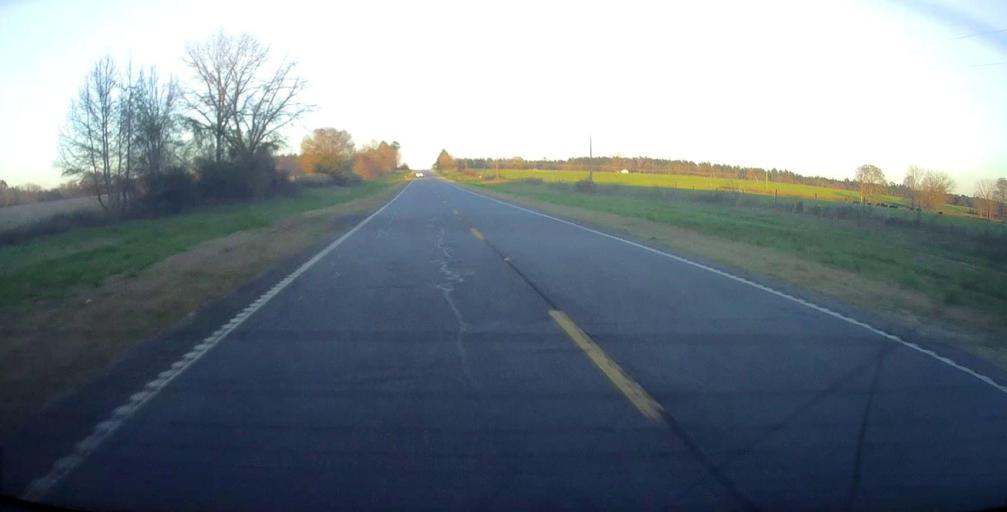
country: US
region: Georgia
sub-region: Dodge County
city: Chester
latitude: 32.2918
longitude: -83.0911
